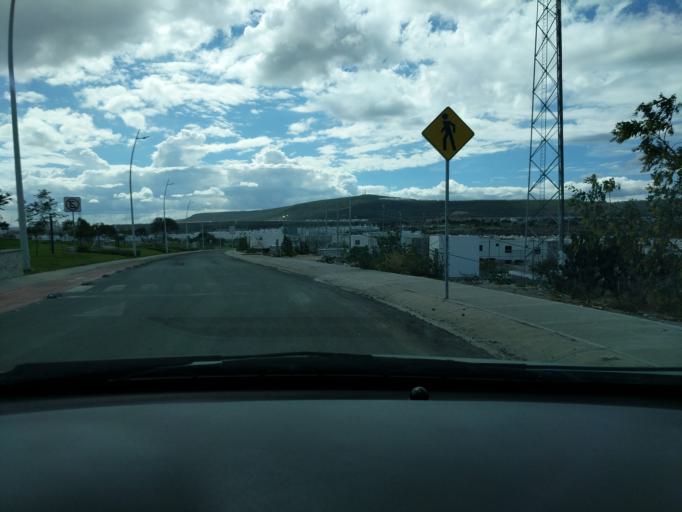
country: MX
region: Queretaro
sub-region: El Marques
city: El Pozo
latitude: 20.6461
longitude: -100.3088
